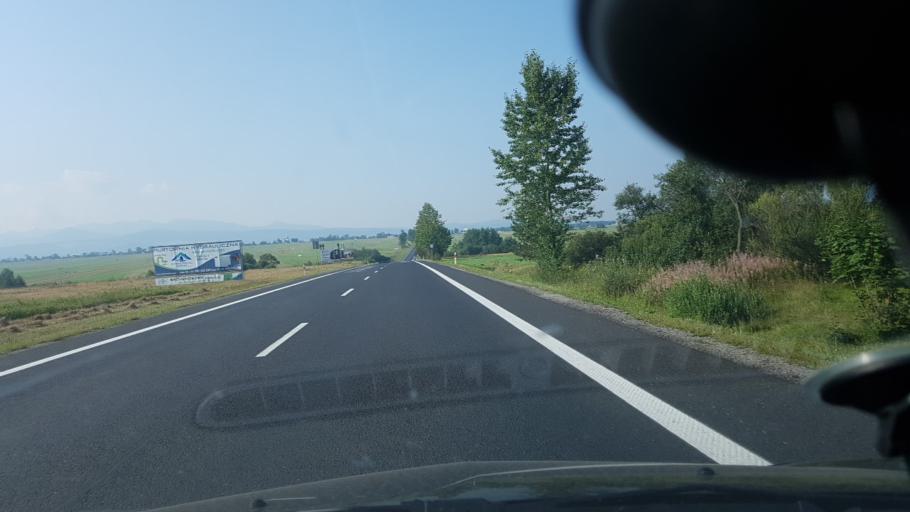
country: PL
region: Lesser Poland Voivodeship
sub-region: Powiat nowotarski
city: Chyzne
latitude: 49.4449
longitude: 19.6842
